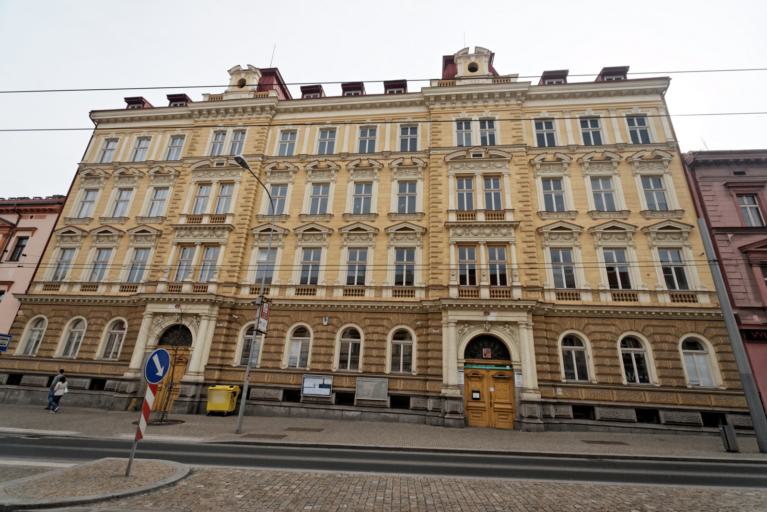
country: CZ
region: Plzensky
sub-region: Okres Plzen-Mesto
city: Pilsen
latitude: 49.7434
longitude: 13.3765
